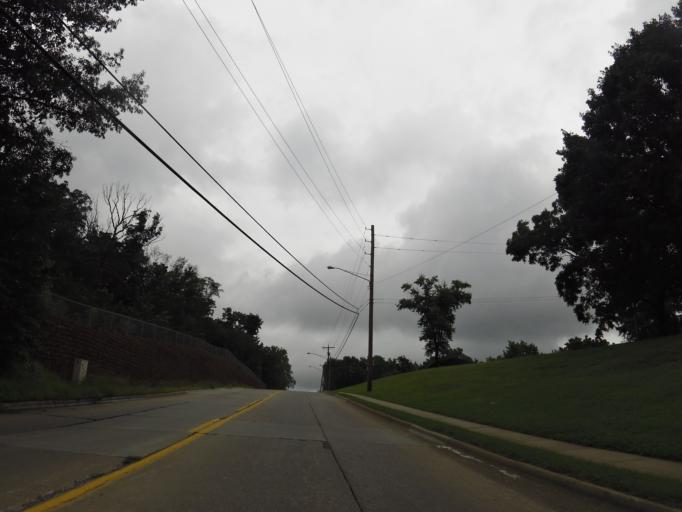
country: US
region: Missouri
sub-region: Cape Girardeau County
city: Cape Girardeau
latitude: 37.3305
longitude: -89.5448
